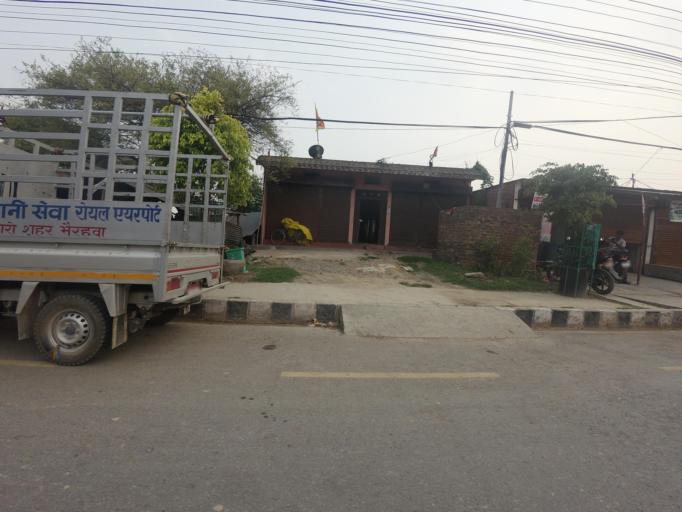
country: NP
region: Western Region
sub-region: Lumbini Zone
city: Bhairahawa
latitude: 27.5083
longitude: 83.4239
